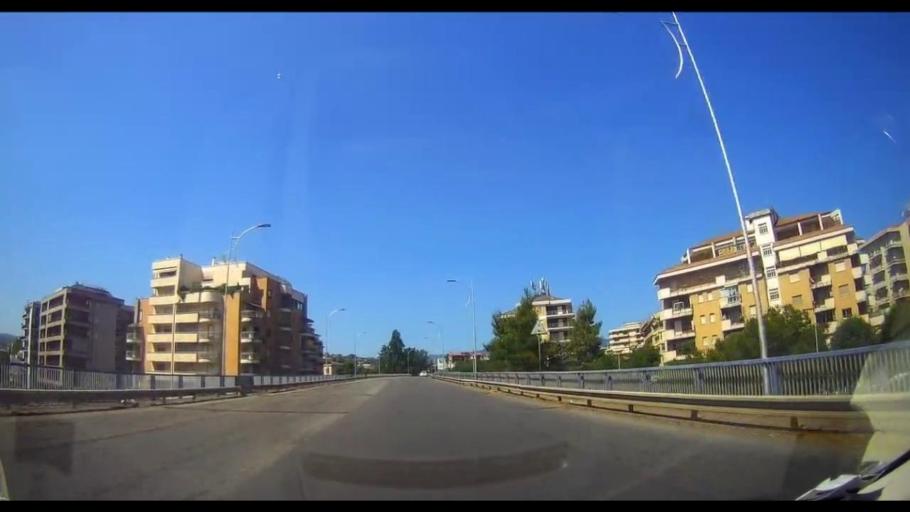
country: IT
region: Calabria
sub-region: Provincia di Cosenza
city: Cosenza
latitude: 39.3121
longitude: 16.2549
